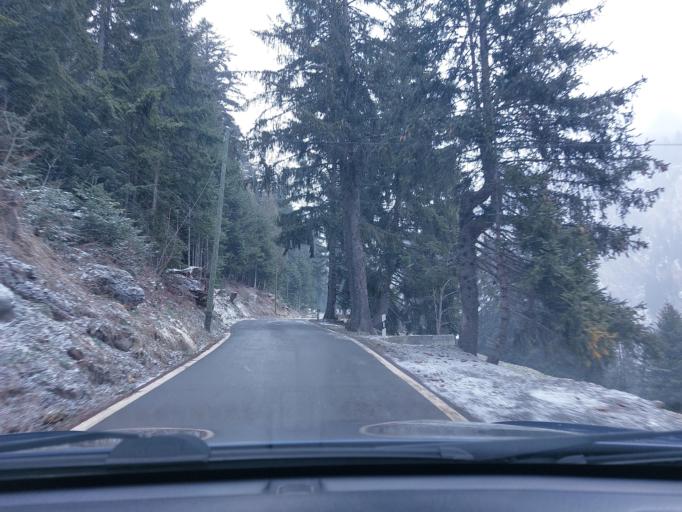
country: CH
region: Valais
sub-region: Sion District
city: Saviese
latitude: 46.2945
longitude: 7.3247
